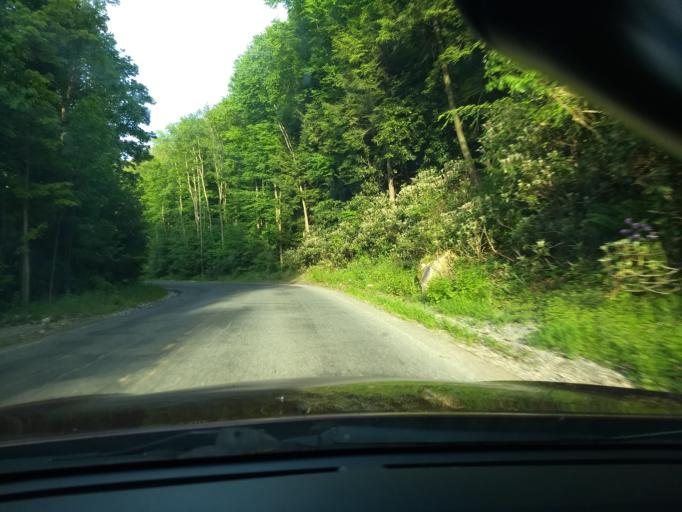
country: US
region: Pennsylvania
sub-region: Cambria County
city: Gallitzin
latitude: 40.4996
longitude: -78.5104
